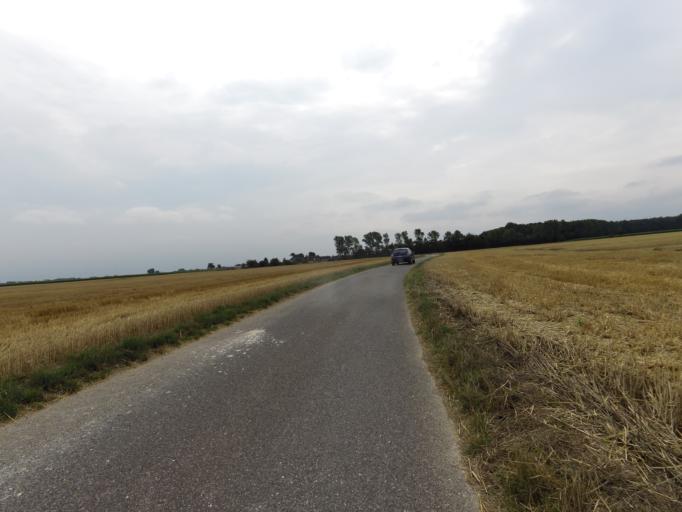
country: DE
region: North Rhine-Westphalia
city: Geilenkirchen
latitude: 51.0096
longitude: 6.1484
